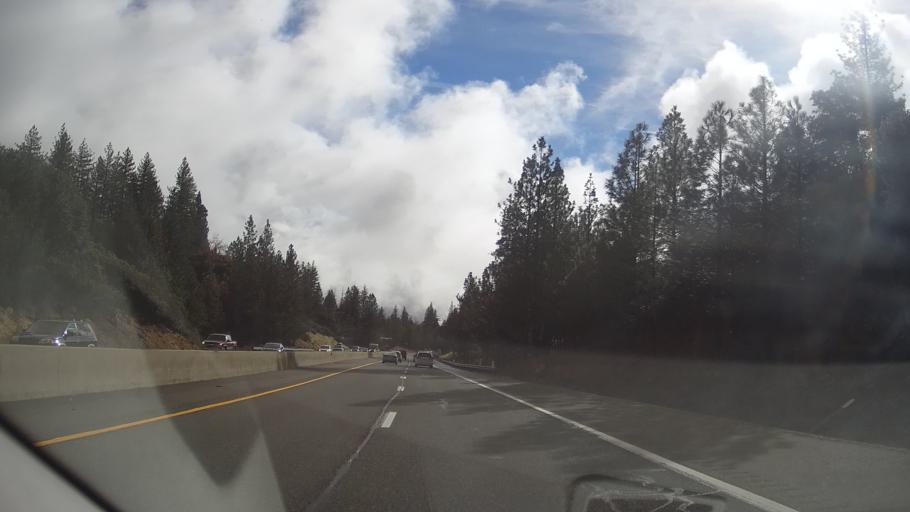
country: US
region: California
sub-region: Placer County
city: Colfax
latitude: 39.1652
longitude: -120.8759
